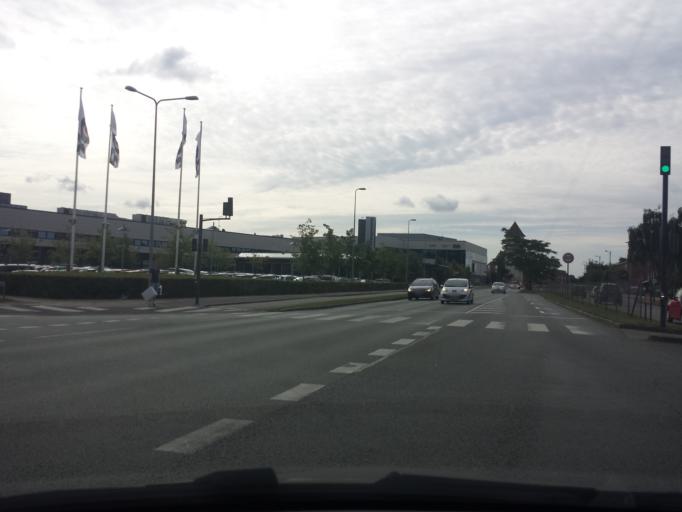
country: DK
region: Capital Region
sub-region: Rodovre Kommune
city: Rodovre
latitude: 55.6806
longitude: 12.4535
